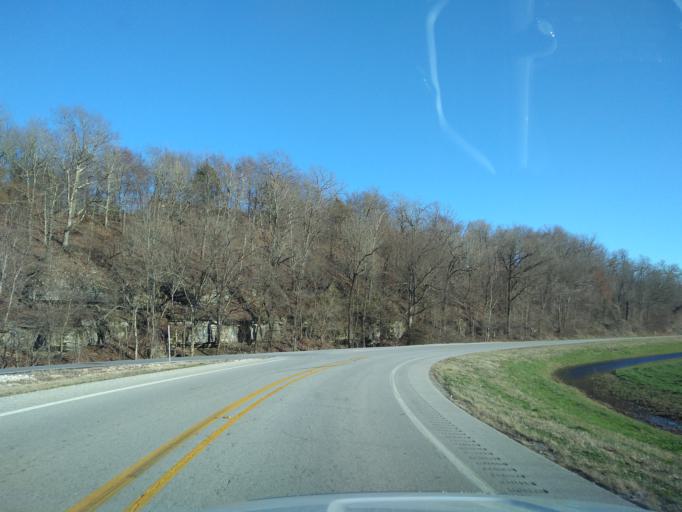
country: US
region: Arkansas
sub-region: Washington County
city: Farmington
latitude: 36.1027
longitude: -94.3416
